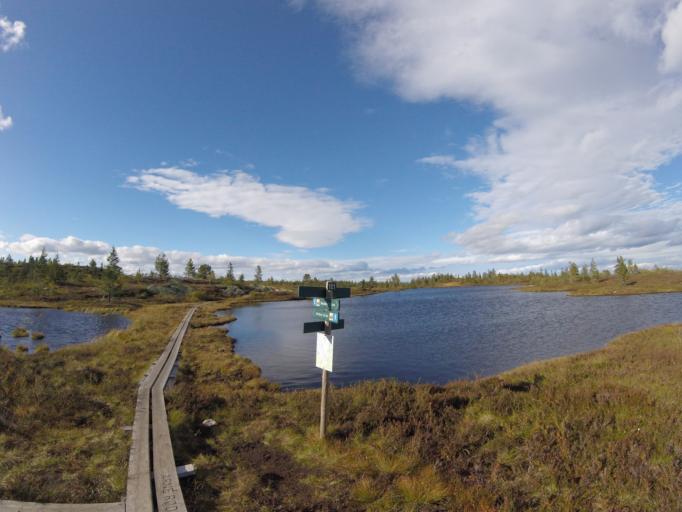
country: NO
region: Buskerud
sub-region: Flesberg
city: Lampeland
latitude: 59.7725
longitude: 9.4070
